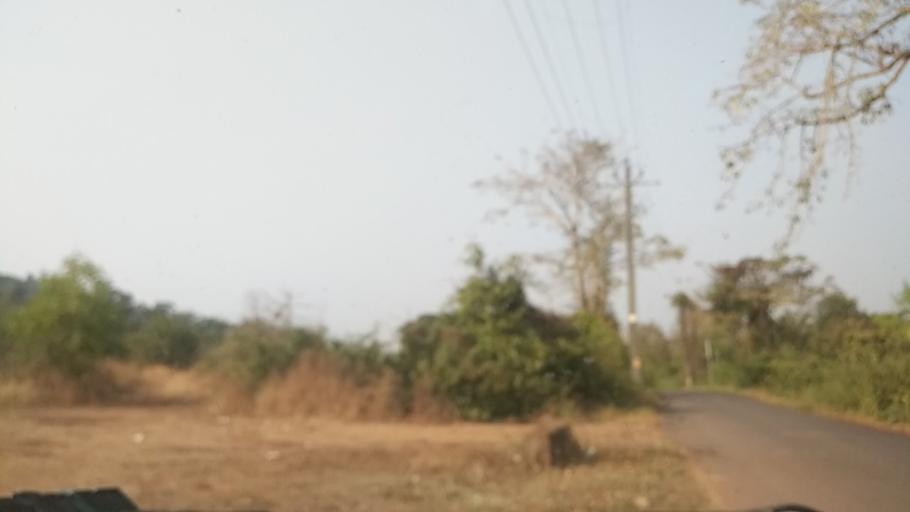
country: IN
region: Goa
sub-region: South Goa
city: Raia
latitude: 15.3241
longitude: 73.9522
